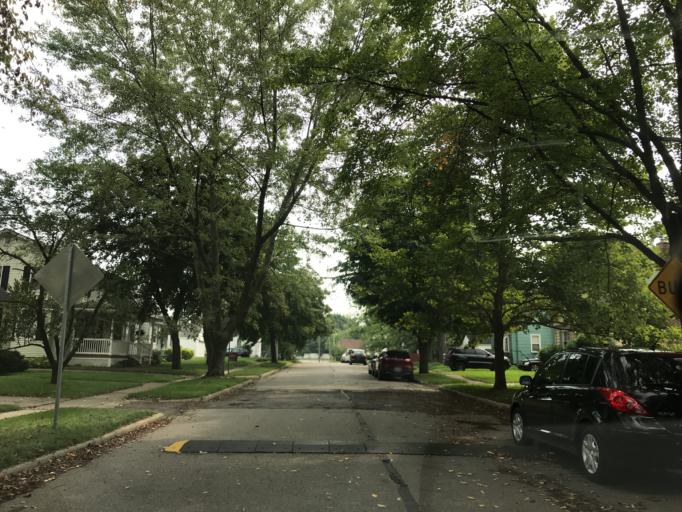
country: US
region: Michigan
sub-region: Washtenaw County
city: Ypsilanti
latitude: 42.2508
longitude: -83.6067
